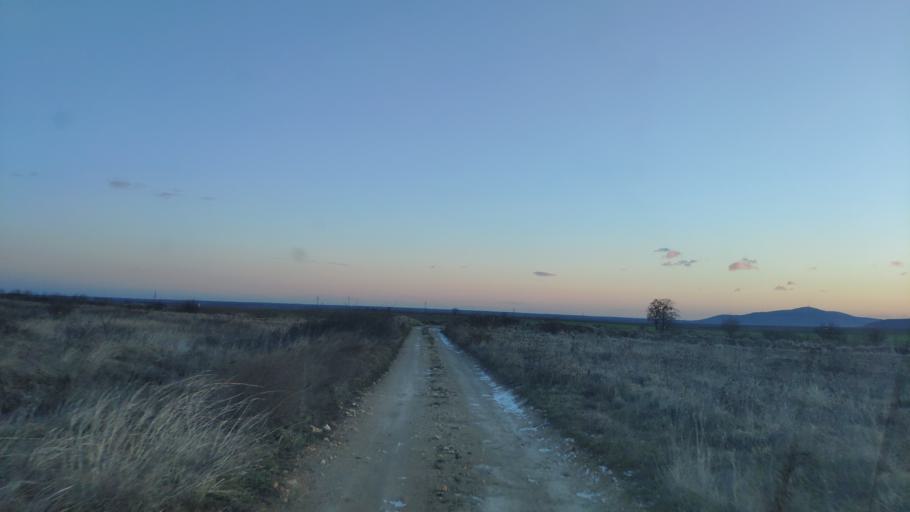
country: HU
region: Borsod-Abauj-Zemplen
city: Olaszliszka
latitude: 48.2672
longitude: 21.4012
